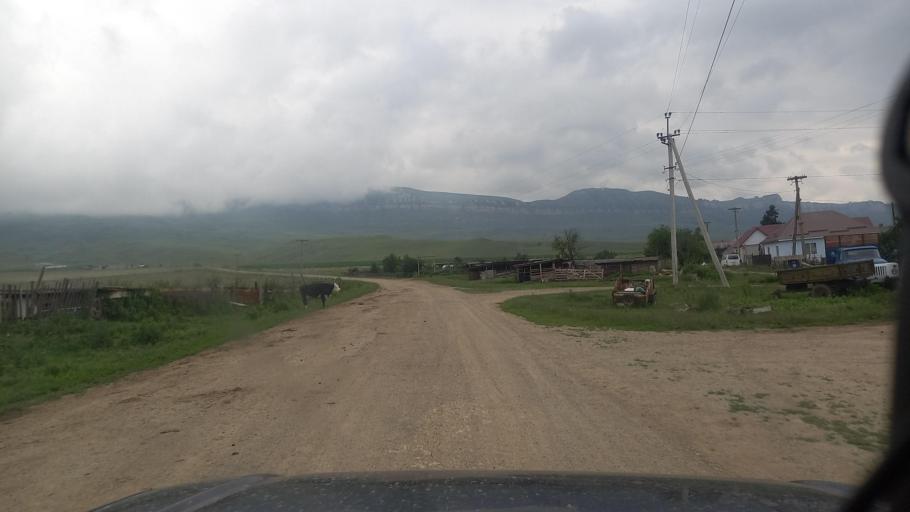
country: RU
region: Karachayevo-Cherkesiya
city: Pregradnaya
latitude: 43.9884
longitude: 41.1957
